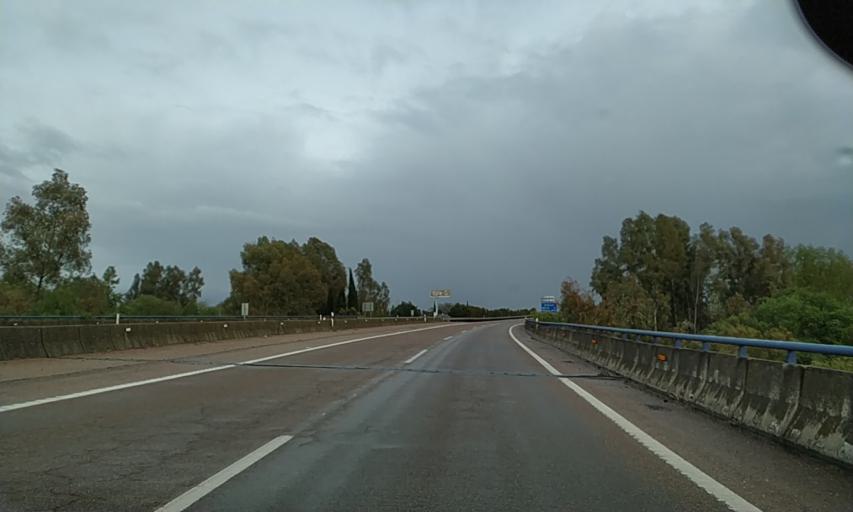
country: ES
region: Extremadura
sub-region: Provincia de Badajoz
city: Badajoz
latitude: 38.9197
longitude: -6.9573
